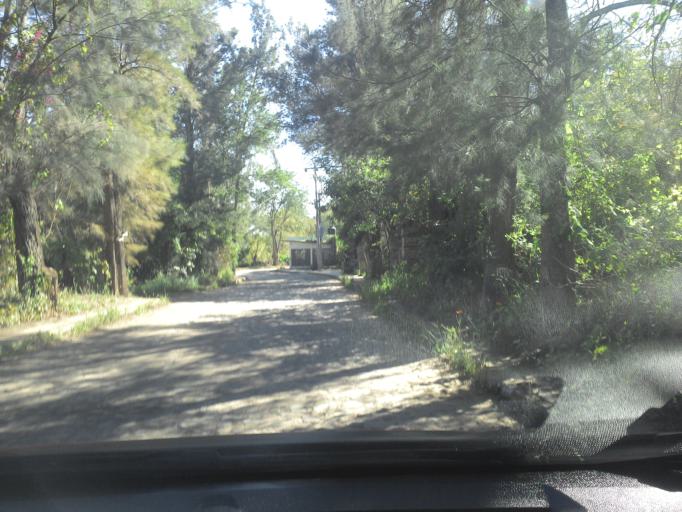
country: MX
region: Jalisco
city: Teuchitlan
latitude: 20.6904
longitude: -103.8440
